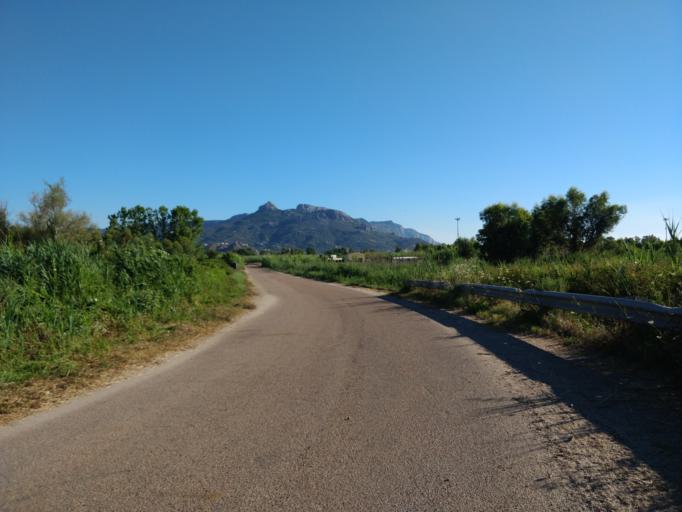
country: IT
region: Sardinia
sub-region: Provincia di Ogliastra
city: Girasole
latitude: 39.9583
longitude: 9.6774
